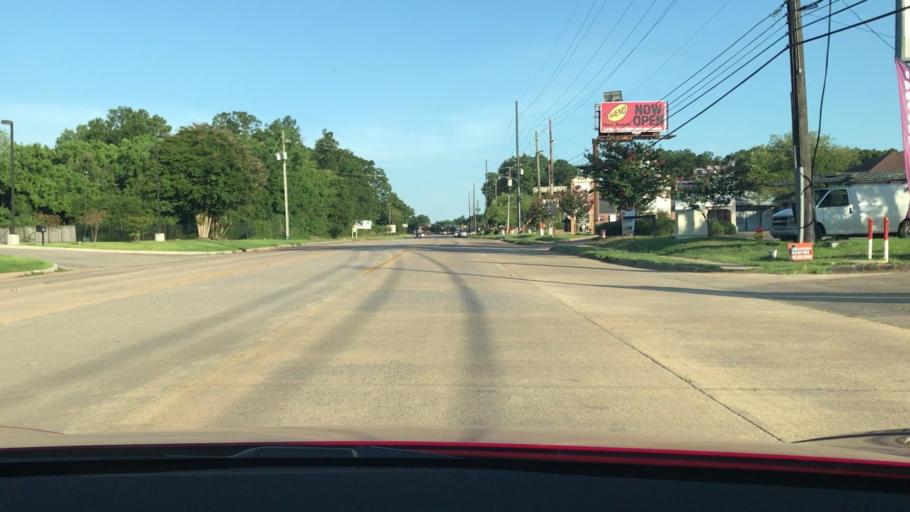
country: US
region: Louisiana
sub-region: Bossier Parish
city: Bossier City
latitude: 32.4249
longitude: -93.7397
